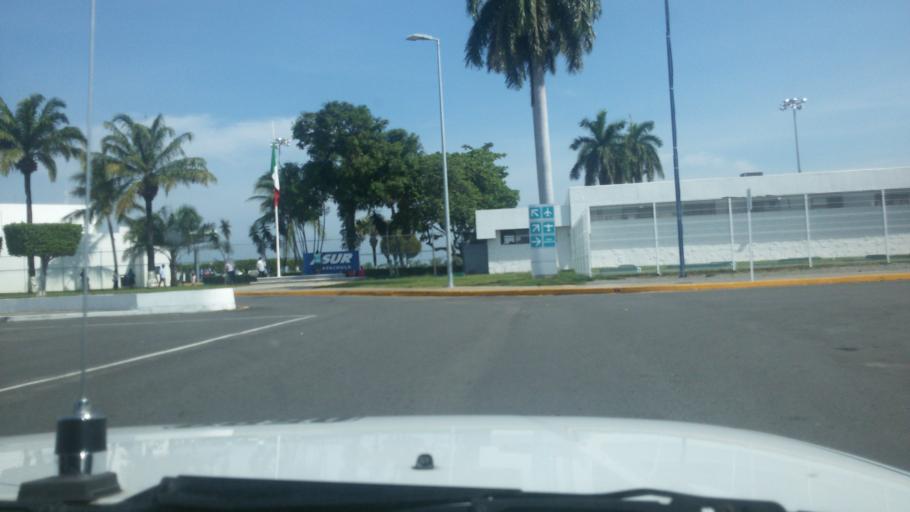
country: MX
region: Chiapas
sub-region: Tapachula
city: Congregacion Reforma
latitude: 14.7904
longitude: -92.3679
